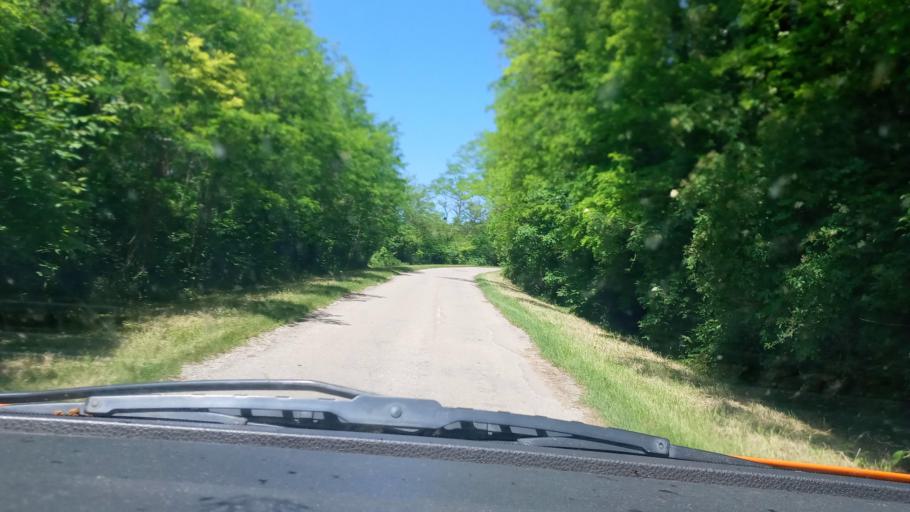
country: HU
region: Somogy
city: Kadarkut
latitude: 46.1840
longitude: 17.7312
